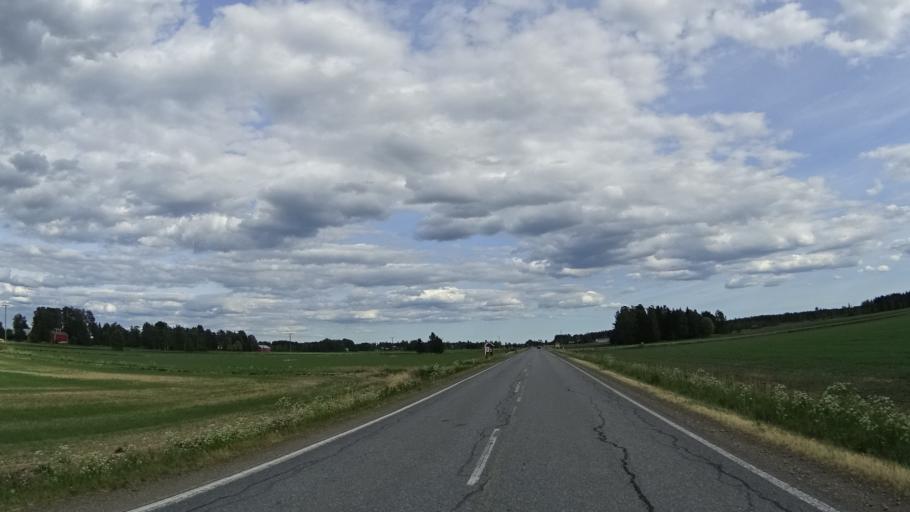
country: FI
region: Pirkanmaa
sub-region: Etelae-Pirkanmaa
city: Urjala
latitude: 60.9490
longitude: 23.5374
